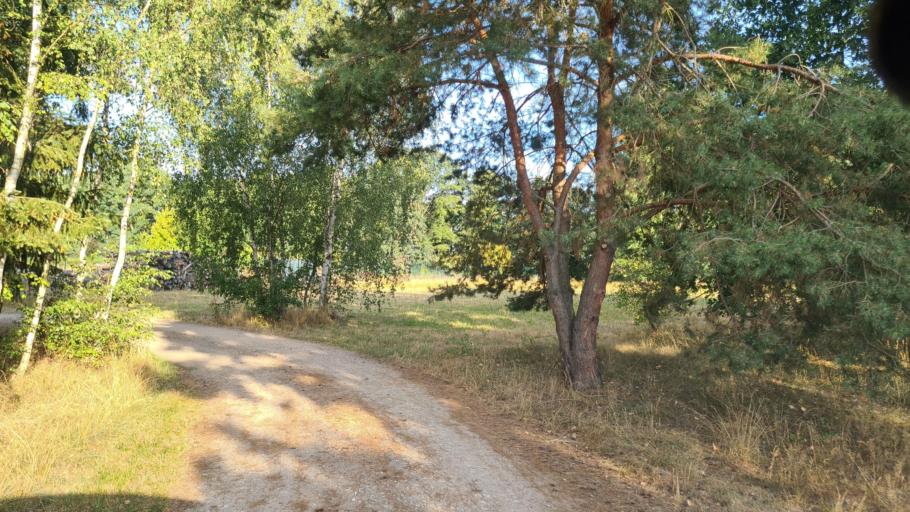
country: DE
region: Brandenburg
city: Juterbog
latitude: 52.0289
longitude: 13.0997
